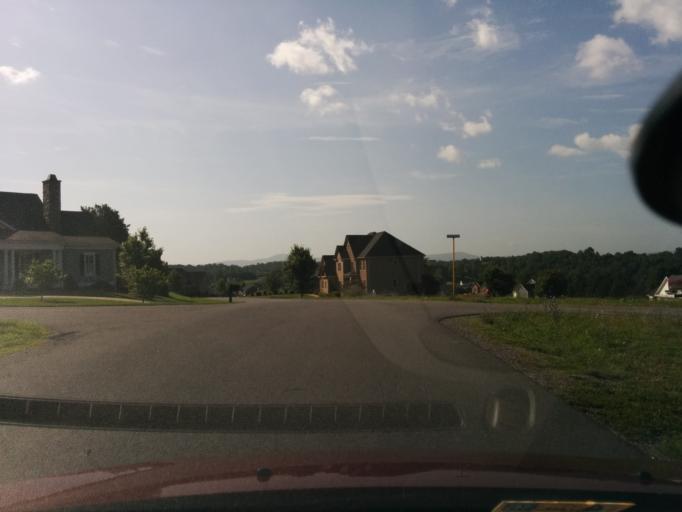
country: US
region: Virginia
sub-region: City of Lexington
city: Lexington
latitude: 37.7713
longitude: -79.4719
